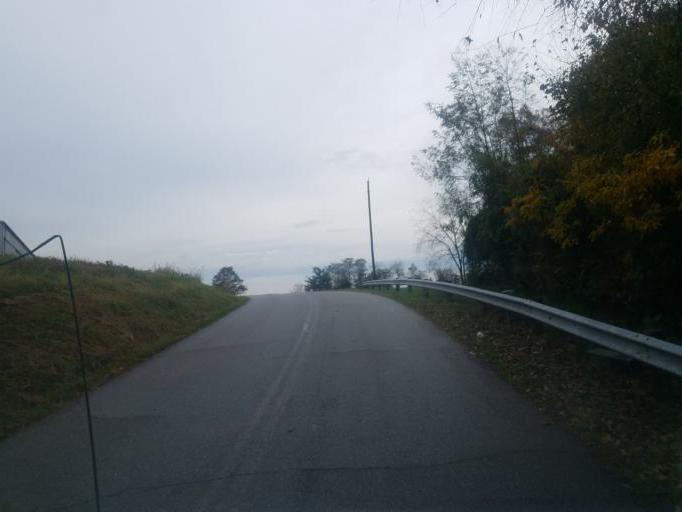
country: US
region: Ohio
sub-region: Washington County
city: Beverly
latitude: 39.5381
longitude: -81.7112
